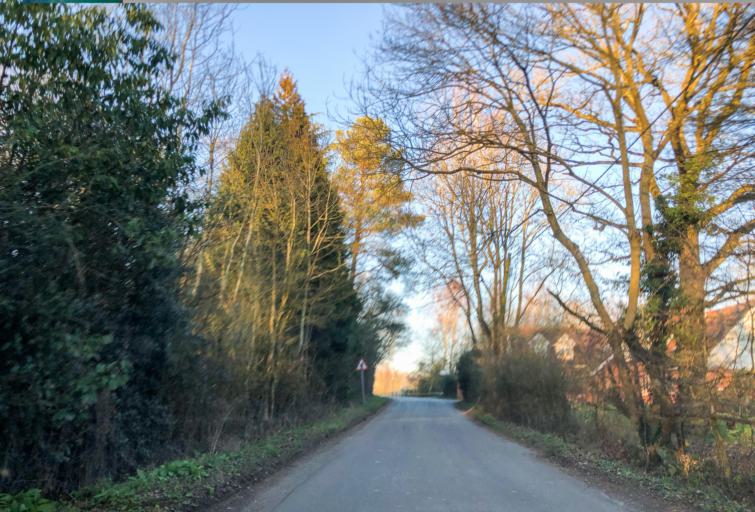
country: GB
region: England
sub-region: Warwickshire
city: Wroxall
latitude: 52.2836
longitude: -1.6656
